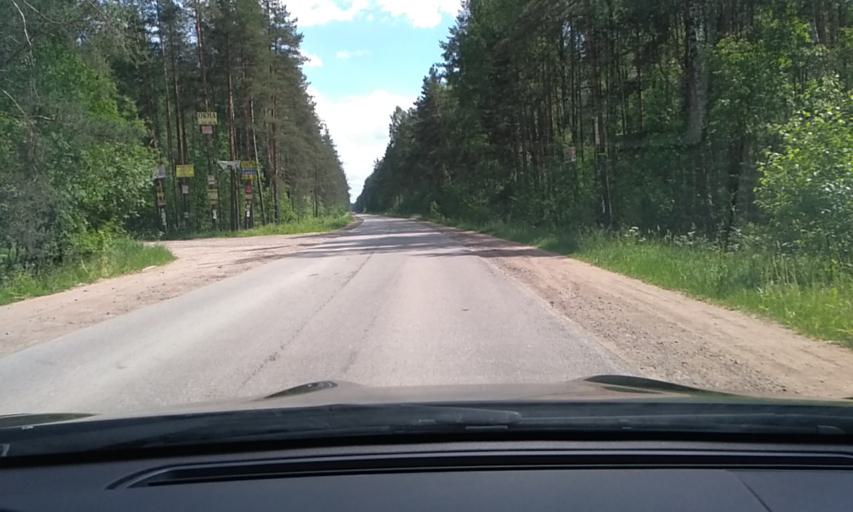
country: RU
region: Leningrad
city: Imeni Sverdlova
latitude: 59.8421
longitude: 30.6908
